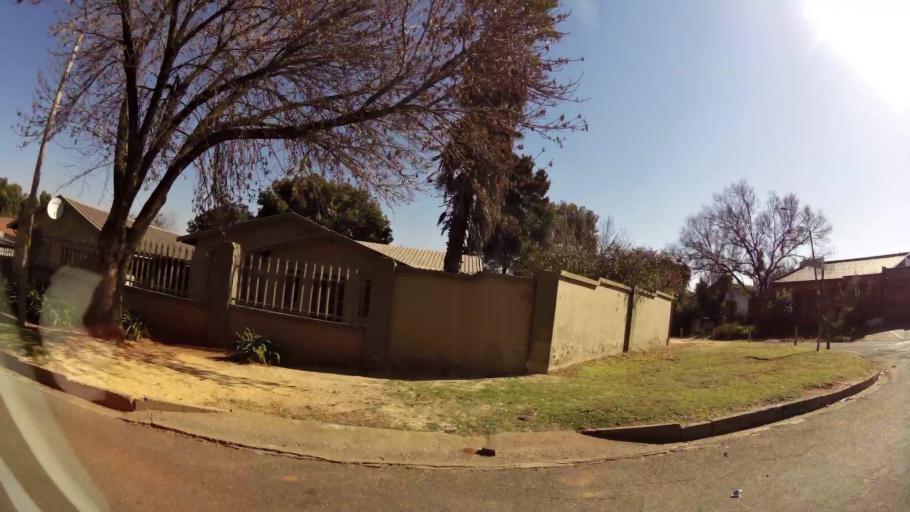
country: ZA
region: Gauteng
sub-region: City of Johannesburg Metropolitan Municipality
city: Modderfontein
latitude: -26.0878
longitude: 28.1848
